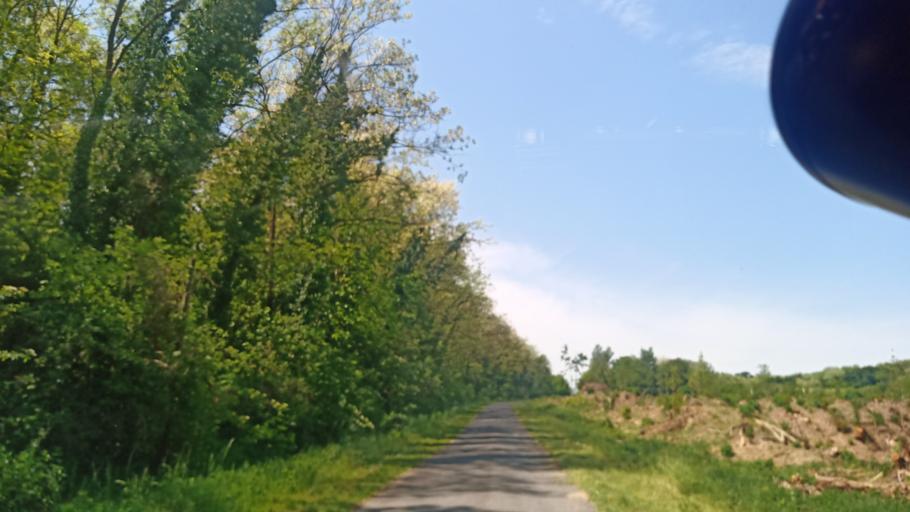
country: HU
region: Zala
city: Zalakomar
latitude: 46.6087
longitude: 17.1147
